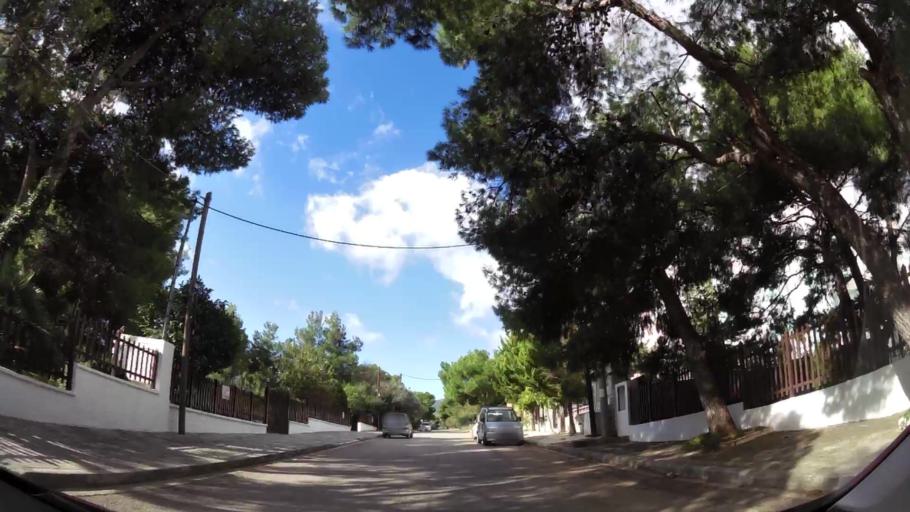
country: GR
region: Attica
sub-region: Nomarchia Anatolikis Attikis
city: Thrakomakedones
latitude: 38.1312
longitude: 23.7555
